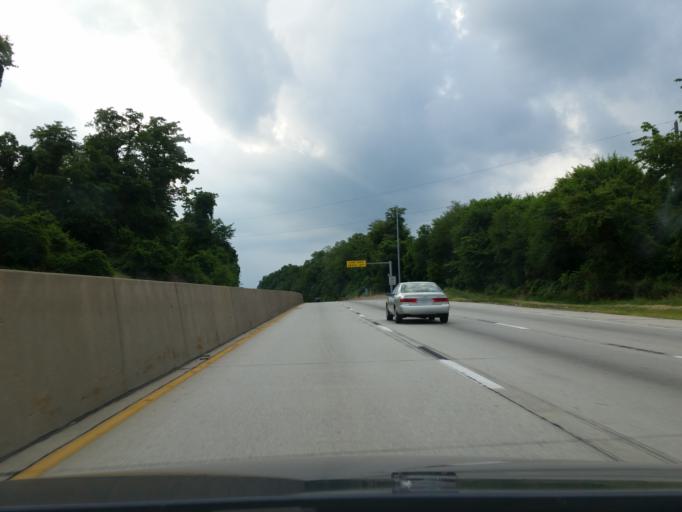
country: US
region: Pennsylvania
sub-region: Dauphin County
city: Steelton
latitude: 40.1908
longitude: -76.8486
